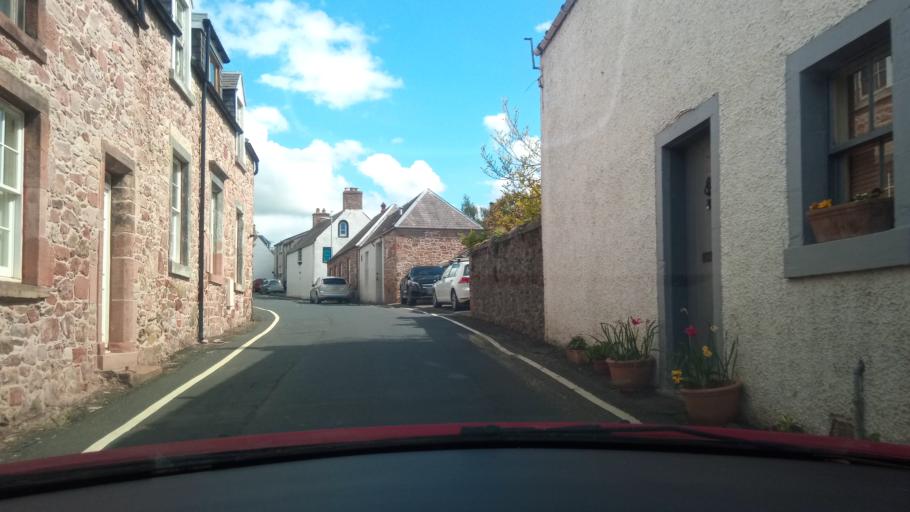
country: GB
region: Scotland
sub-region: The Scottish Borders
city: Newtown St Boswells
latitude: 55.5999
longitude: -2.6958
